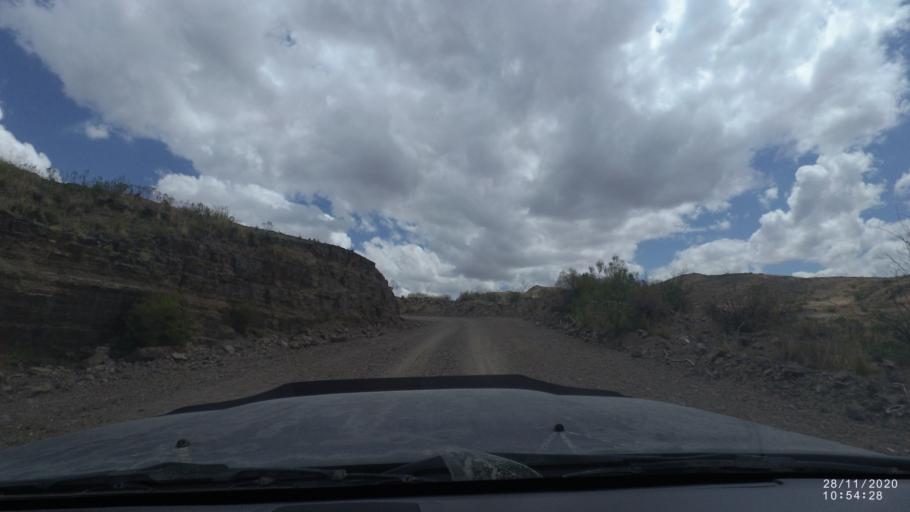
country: BO
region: Cochabamba
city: Capinota
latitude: -17.7779
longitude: -66.1197
